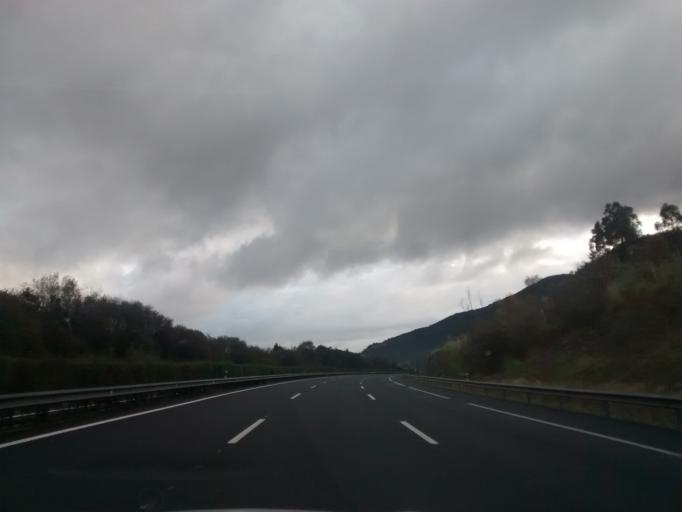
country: ES
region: Cantabria
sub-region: Provincia de Cantabria
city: Entrambasaguas
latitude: 43.4006
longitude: -3.6398
